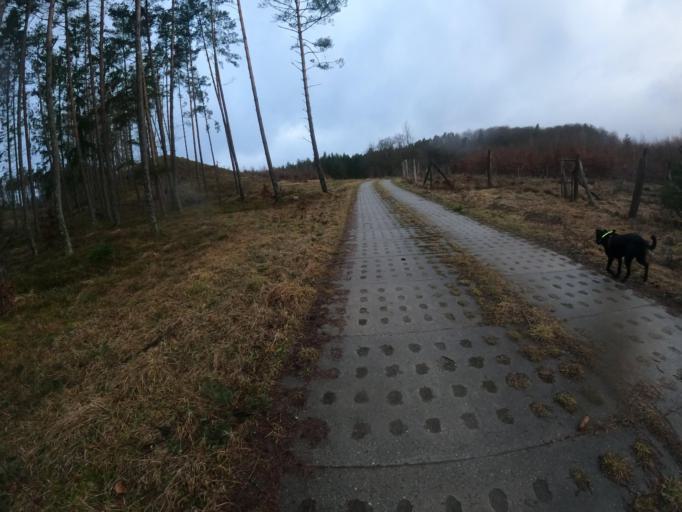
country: PL
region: West Pomeranian Voivodeship
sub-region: Powiat slawienski
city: Slawno
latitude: 54.2818
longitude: 16.7197
